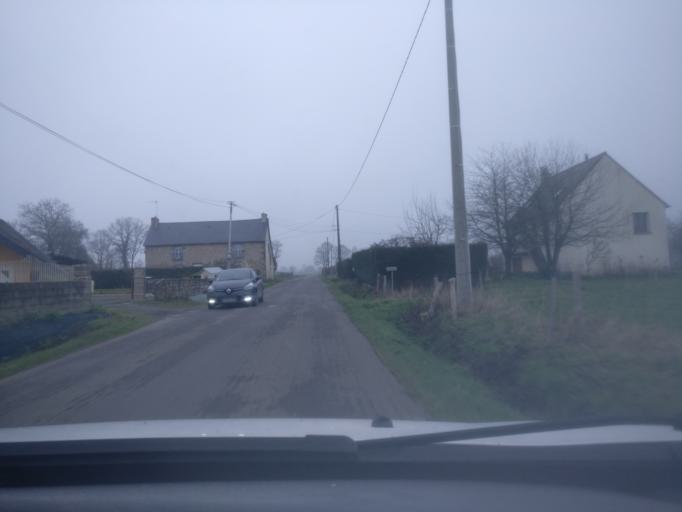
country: FR
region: Brittany
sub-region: Departement d'Ille-et-Vilaine
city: Montreuil-sur-Ille
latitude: 48.3057
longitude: -1.6357
